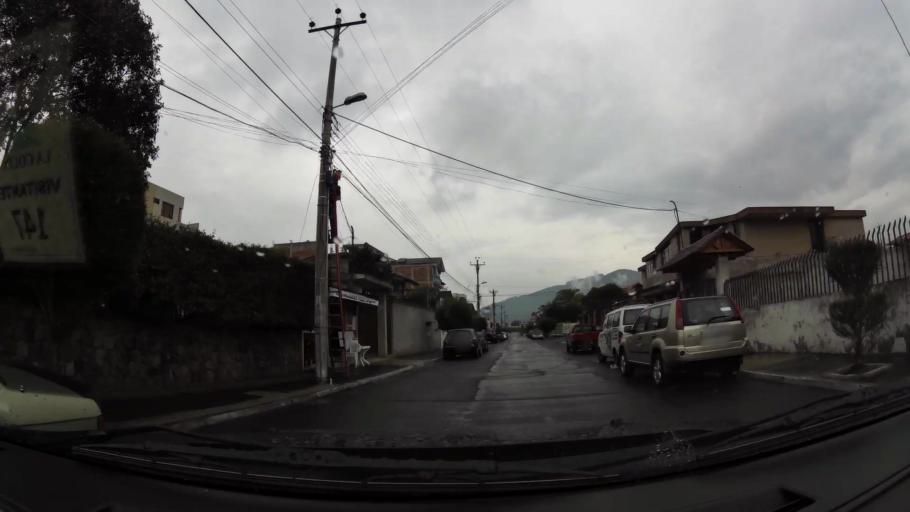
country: EC
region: Pichincha
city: Sangolqui
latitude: -0.3149
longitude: -78.4414
